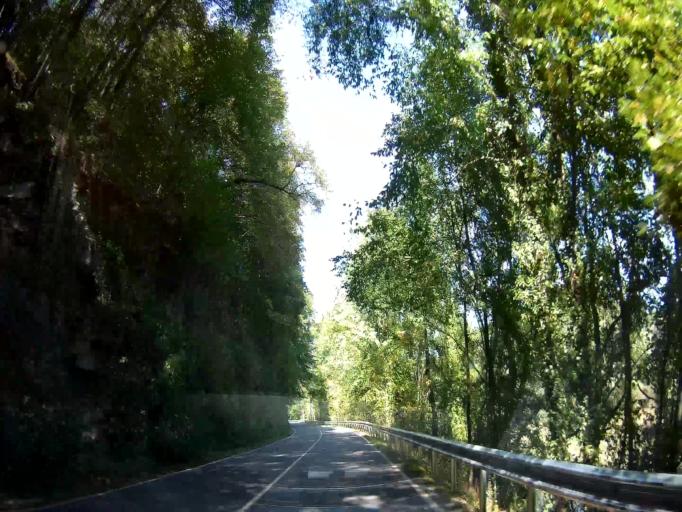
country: BE
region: Wallonia
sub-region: Province du Luxembourg
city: La Roche-en-Ardenne
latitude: 50.1920
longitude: 5.5400
